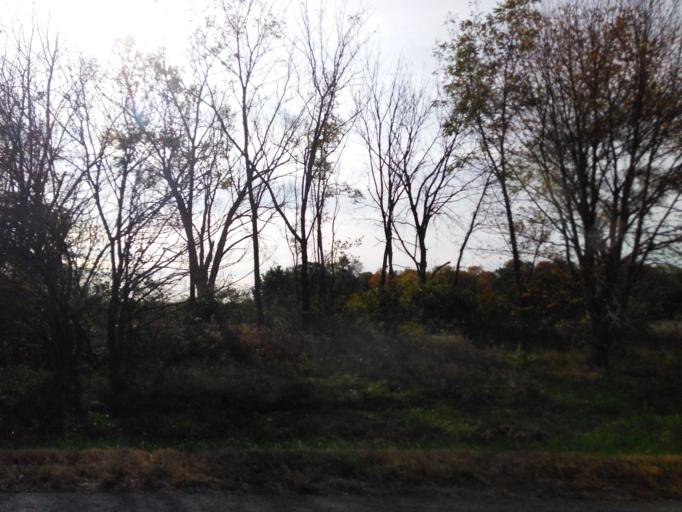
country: US
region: Illinois
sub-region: Madison County
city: Saint Jacob
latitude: 38.7648
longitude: -89.7715
